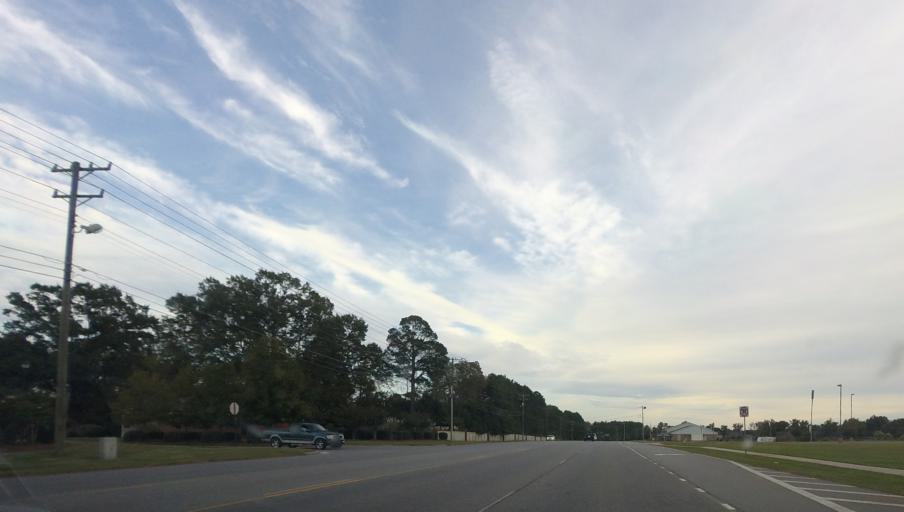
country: US
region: Georgia
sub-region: Houston County
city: Centerville
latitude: 32.5755
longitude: -83.6930
